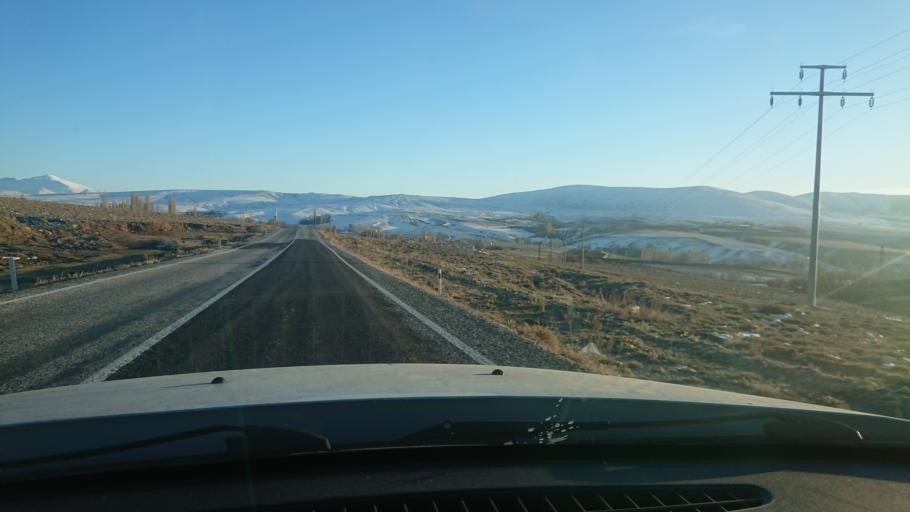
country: TR
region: Aksaray
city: Ortakoy
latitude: 38.7617
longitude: 33.9327
